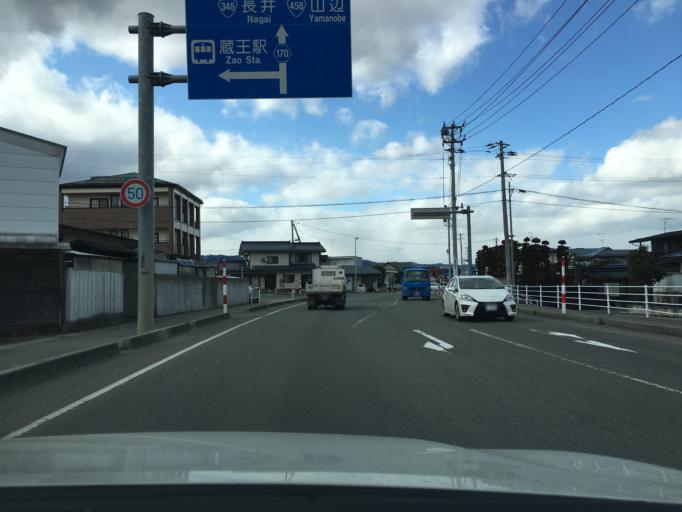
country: JP
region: Yamagata
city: Kaminoyama
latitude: 38.2055
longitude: 140.3091
